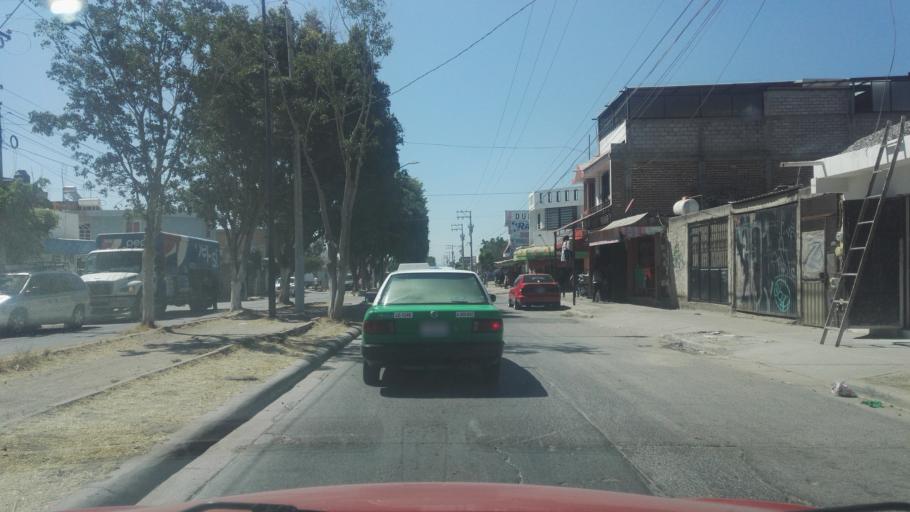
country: MX
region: Guanajuato
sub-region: Leon
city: Fraccionamiento Paraiso Real
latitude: 21.1013
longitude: -101.5865
